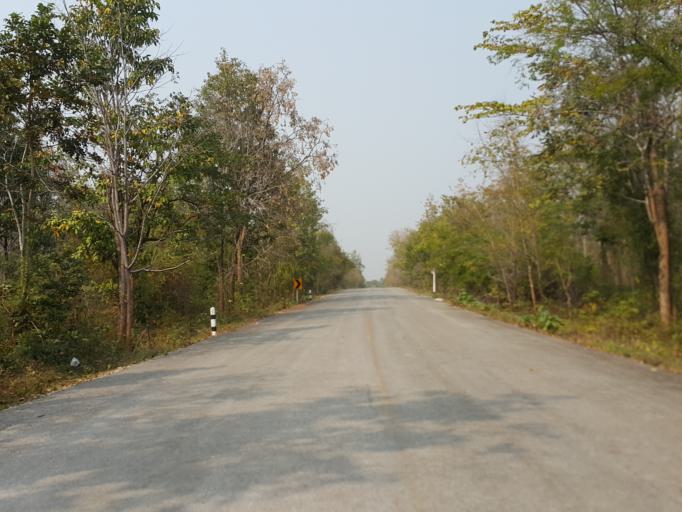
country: TH
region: Lampang
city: Mae Phrik
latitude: 17.4983
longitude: 99.0837
